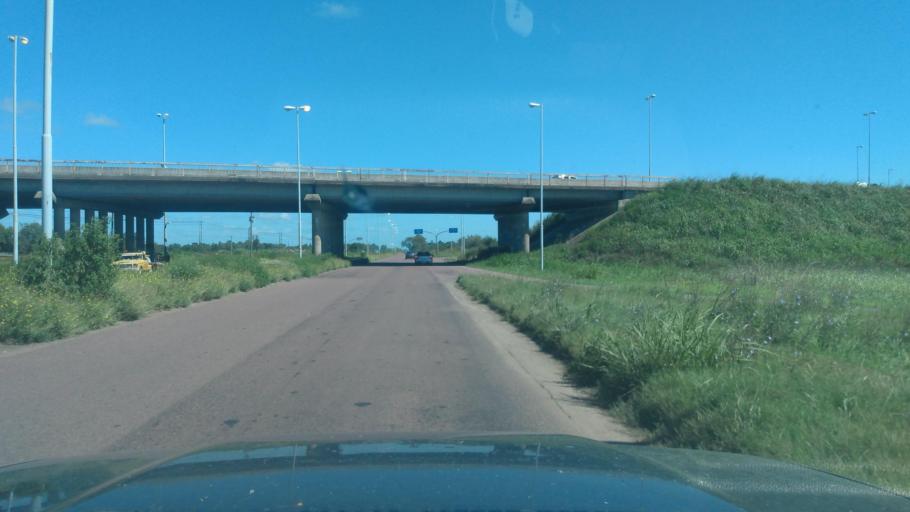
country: AR
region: Buenos Aires
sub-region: Partido de Lujan
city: Lujan
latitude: -34.5888
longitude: -59.0369
